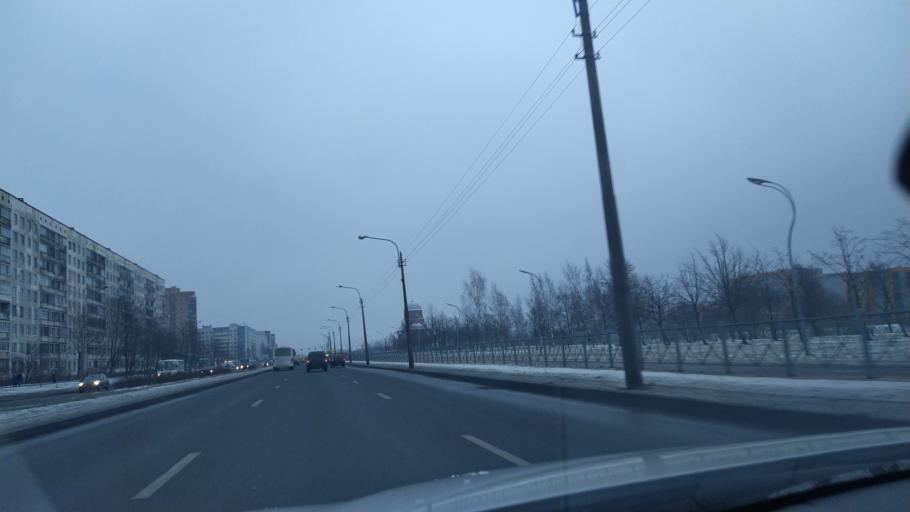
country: RU
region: St.-Petersburg
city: Grazhdanka
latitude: 60.0273
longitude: 30.4047
